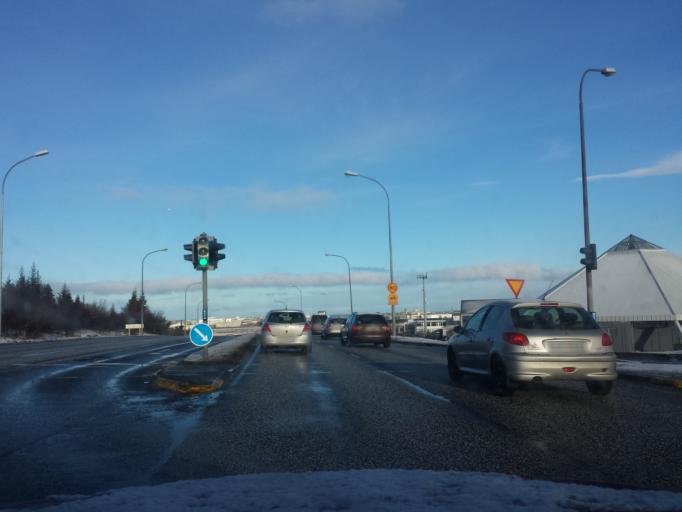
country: IS
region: Capital Region
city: Kopavogur
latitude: 64.1306
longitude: -21.9152
